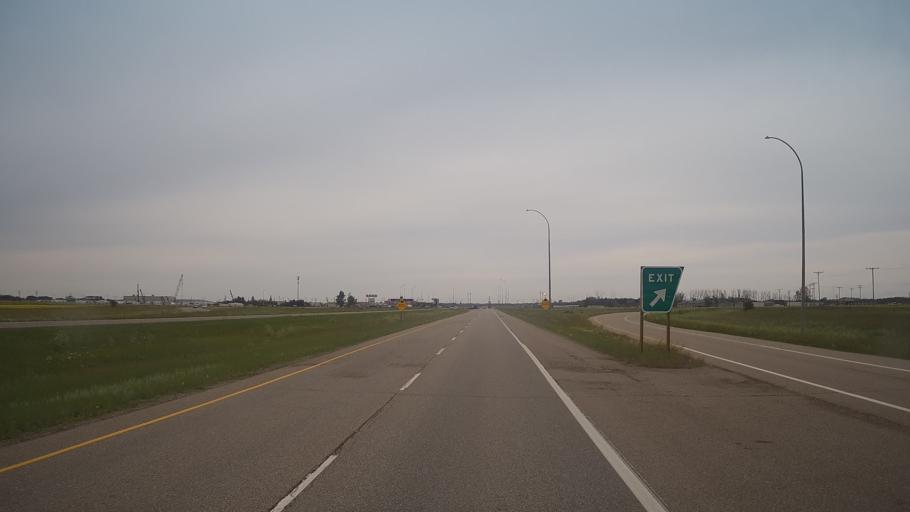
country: CA
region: Saskatchewan
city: Saskatoon
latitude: 52.0495
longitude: -106.5947
